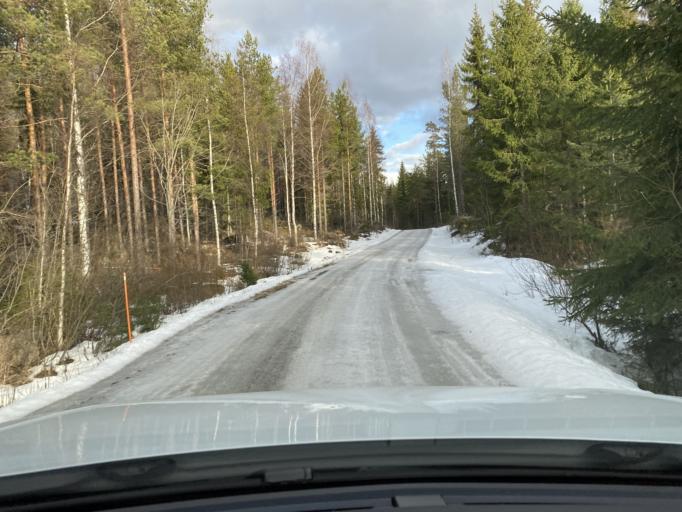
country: FI
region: Pirkanmaa
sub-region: Lounais-Pirkanmaa
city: Mouhijaervi
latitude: 61.4343
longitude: 22.9731
